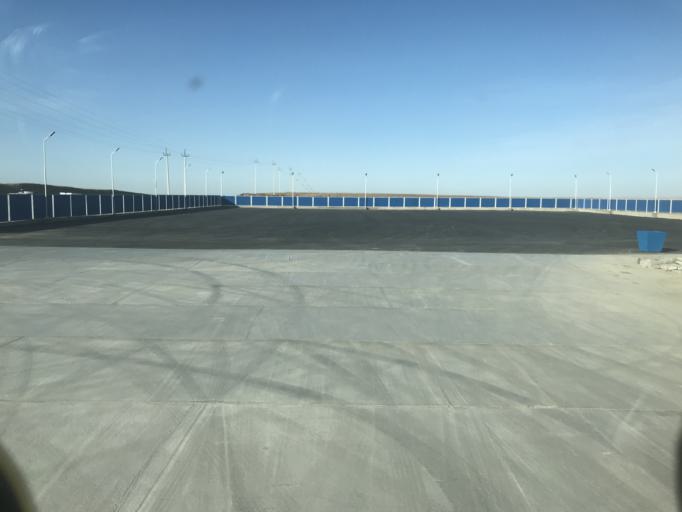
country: KZ
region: Ongtustik Qazaqstan
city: Temirlanovka
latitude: 42.5707
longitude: 69.3111
